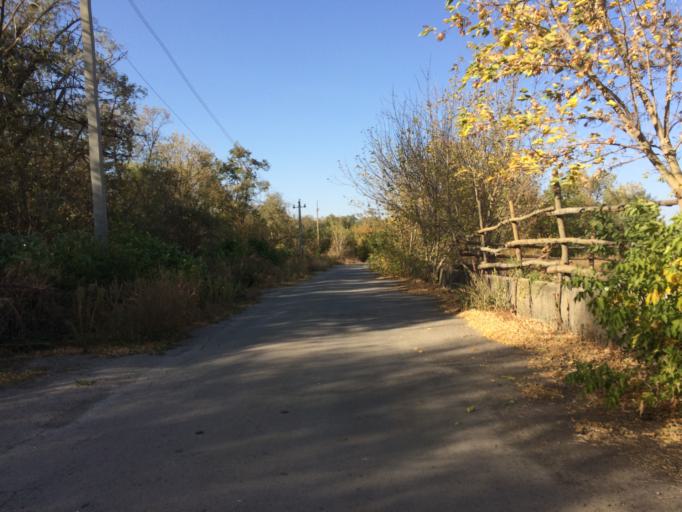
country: RU
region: Rostov
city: Gigant
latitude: 46.5205
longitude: 41.1937
